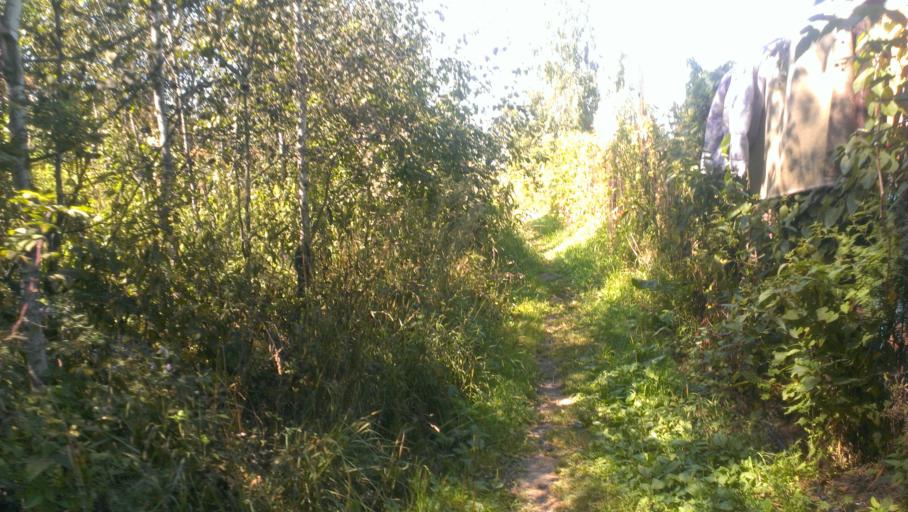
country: RU
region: Altai Krai
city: Nauchnyy Gorodok
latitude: 53.4240
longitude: 83.5071
